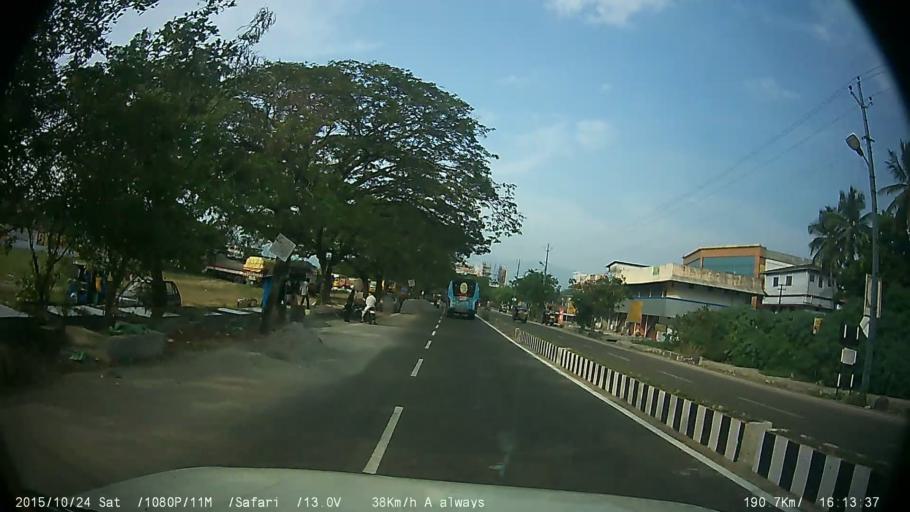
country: IN
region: Kerala
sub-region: Palakkad district
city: Palakkad
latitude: 10.7706
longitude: 76.6620
